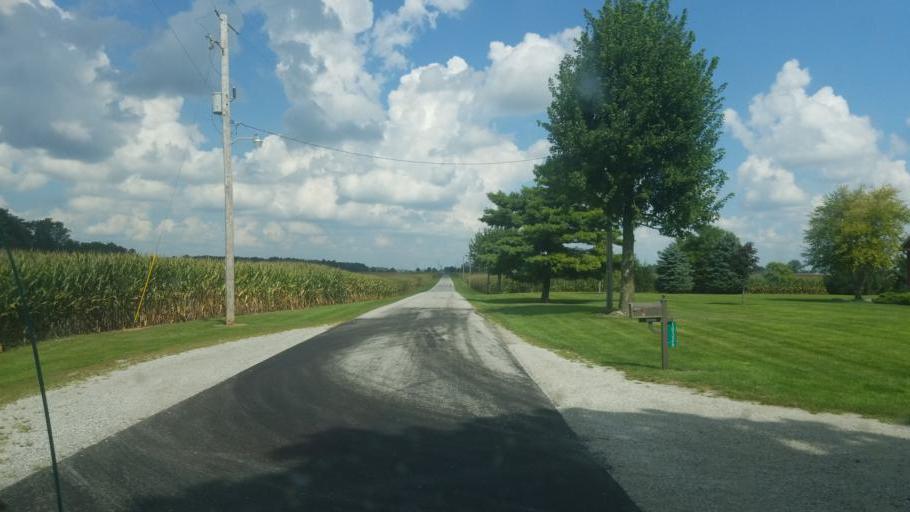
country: US
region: Ohio
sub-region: Hardin County
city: Kenton
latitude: 40.6684
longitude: -83.5621
